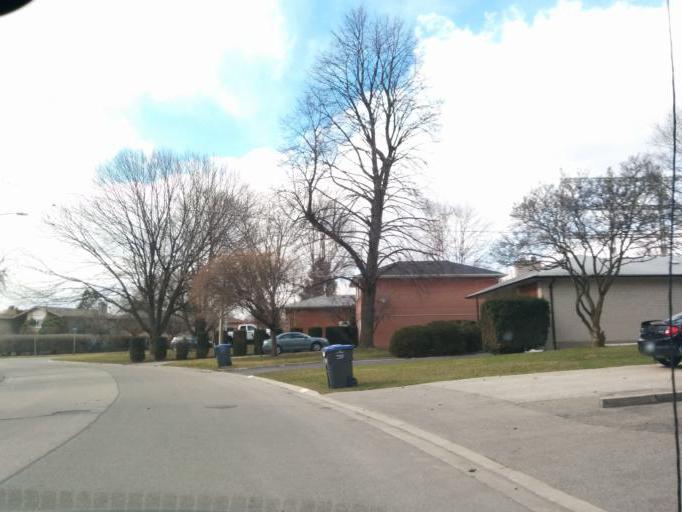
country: CA
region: Ontario
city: Etobicoke
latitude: 43.5859
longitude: -79.5696
